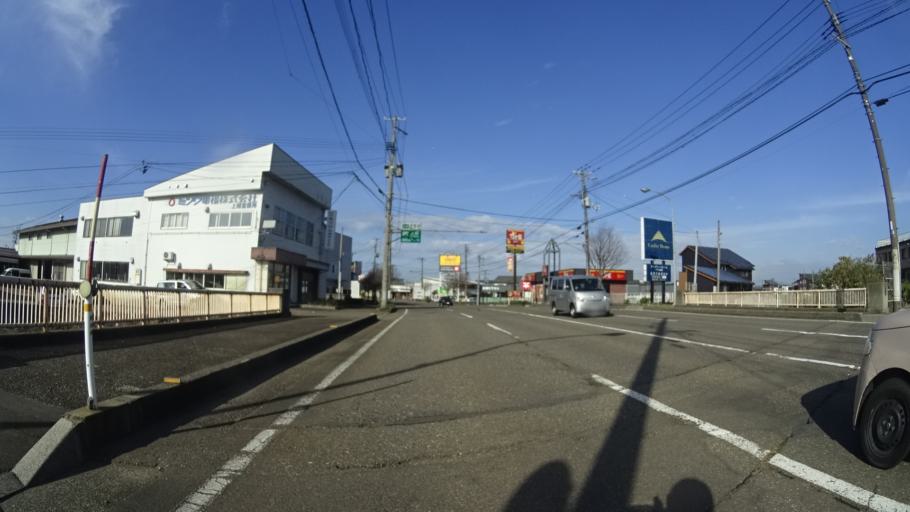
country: JP
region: Niigata
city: Joetsu
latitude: 37.1212
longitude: 138.2519
